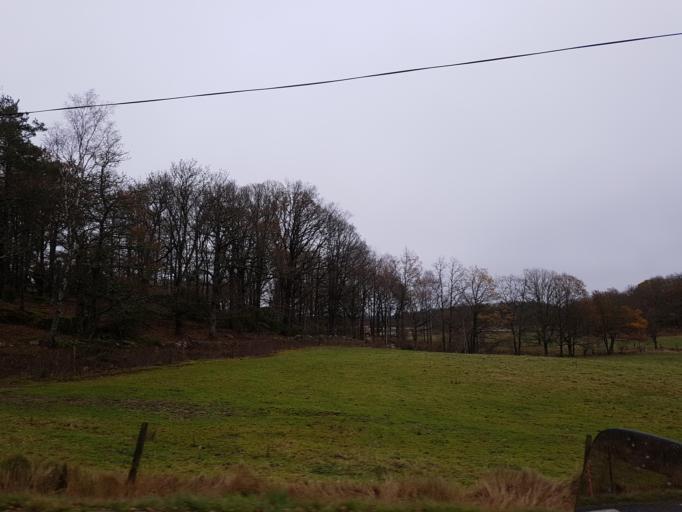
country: SE
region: Vaestra Goetaland
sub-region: Orust
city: Henan
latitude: 58.1616
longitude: 11.7312
